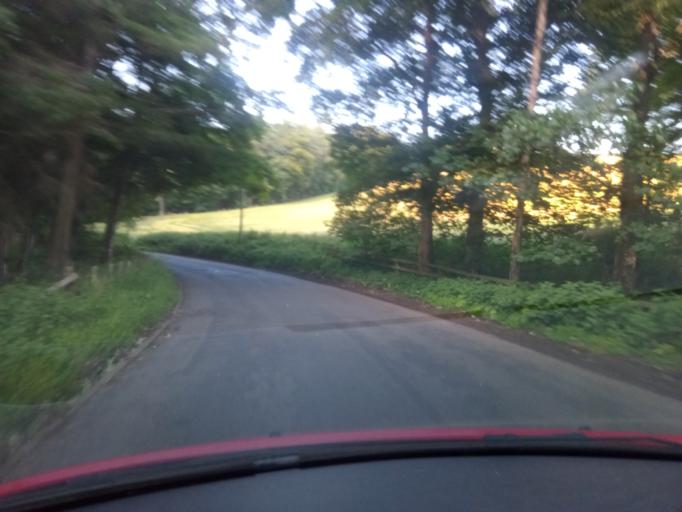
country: GB
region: Scotland
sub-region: The Scottish Borders
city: Selkirk
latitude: 55.5176
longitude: -2.9242
